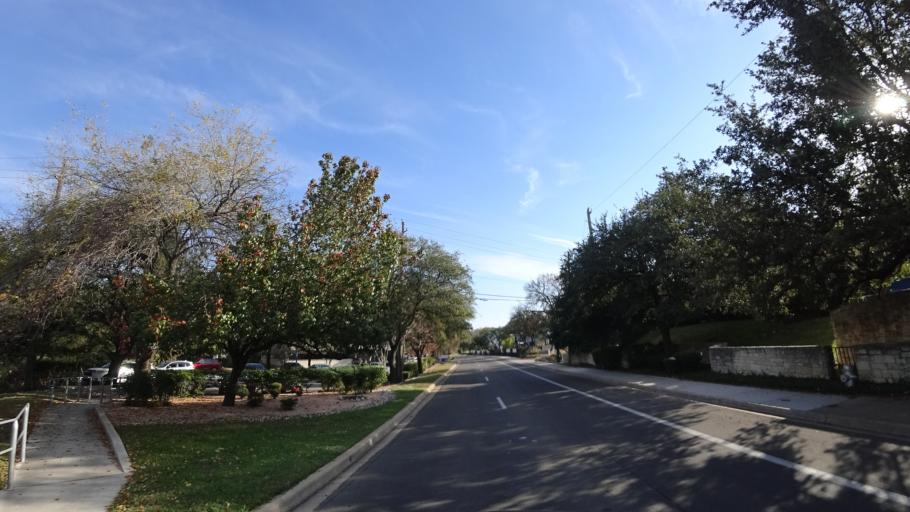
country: US
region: Texas
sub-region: Williamson County
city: Jollyville
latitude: 30.3695
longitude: -97.7550
